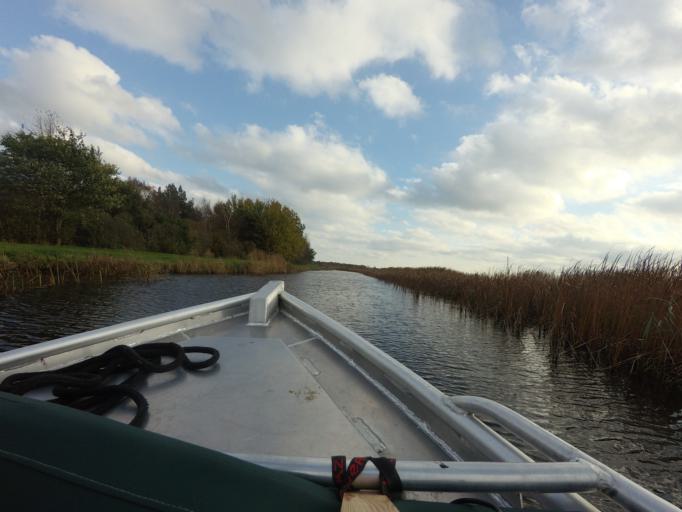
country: NL
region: Overijssel
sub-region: Gemeente Steenwijkerland
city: Blokzijl
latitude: 52.7487
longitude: 5.9692
